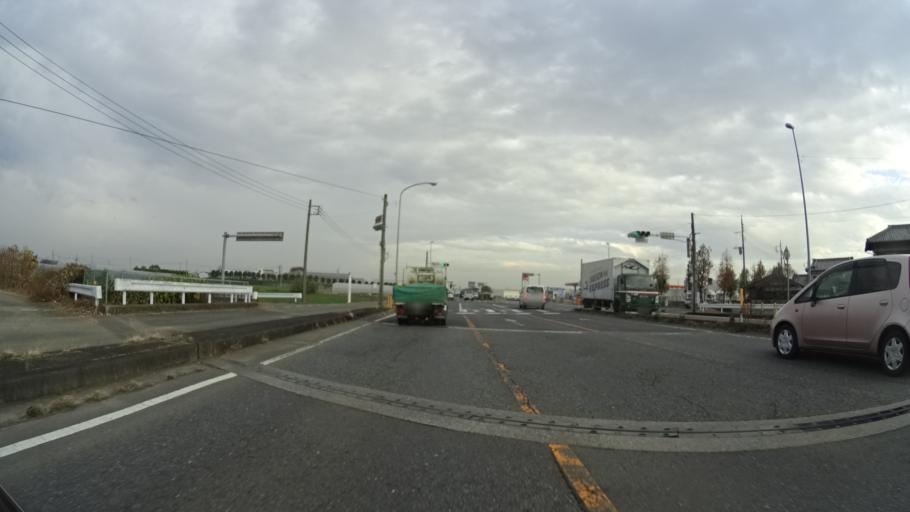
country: JP
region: Gunma
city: Isesaki
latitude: 36.3599
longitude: 139.1969
